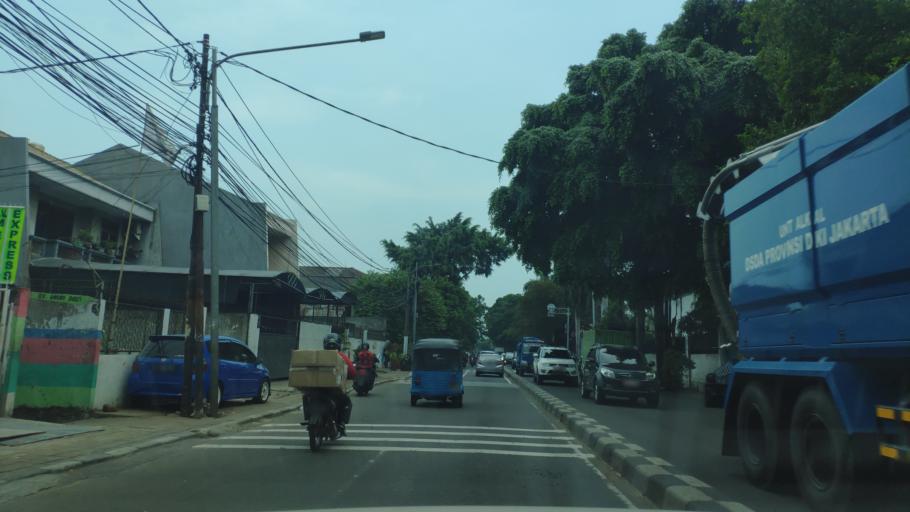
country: ID
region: Jakarta Raya
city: Jakarta
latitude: -6.1892
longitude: 106.8027
